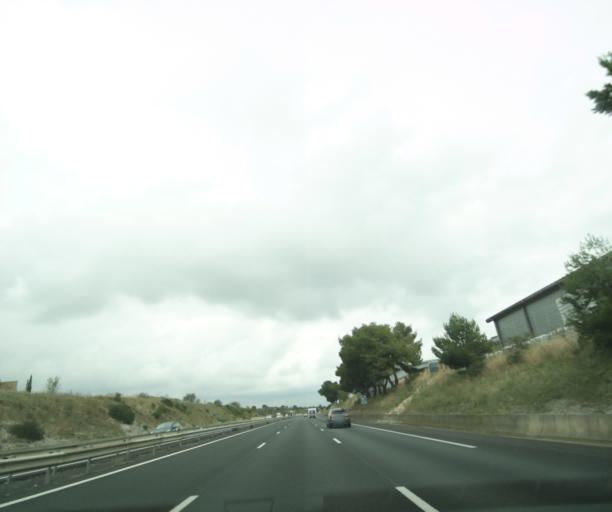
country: FR
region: Languedoc-Roussillon
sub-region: Departement de l'Herault
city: Meze
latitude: 43.4439
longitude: 3.5741
